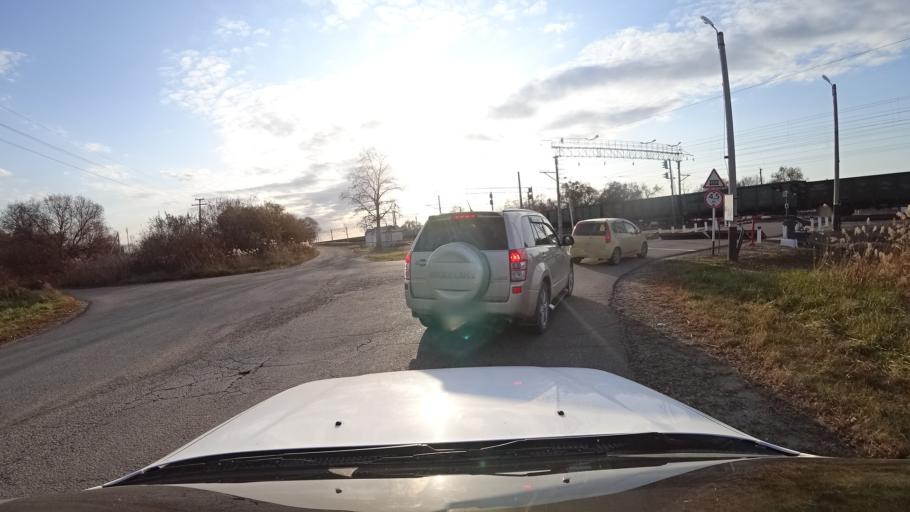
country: RU
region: Primorskiy
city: Lazo
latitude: 45.8234
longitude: 133.6148
